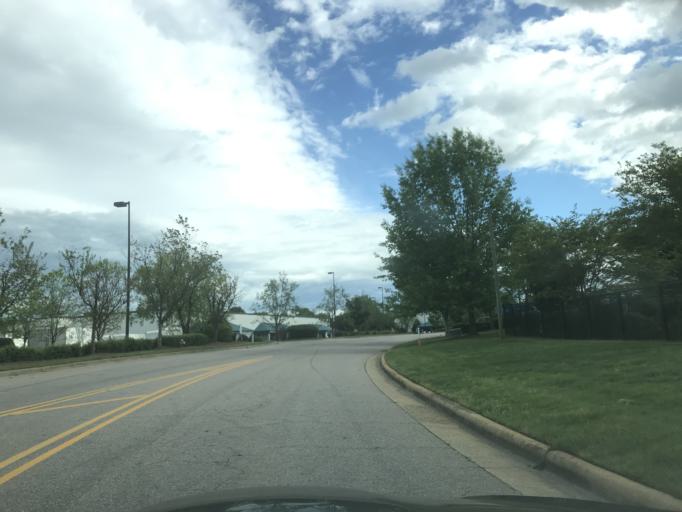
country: US
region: North Carolina
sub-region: Wake County
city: Raleigh
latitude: 35.8107
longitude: -78.5963
